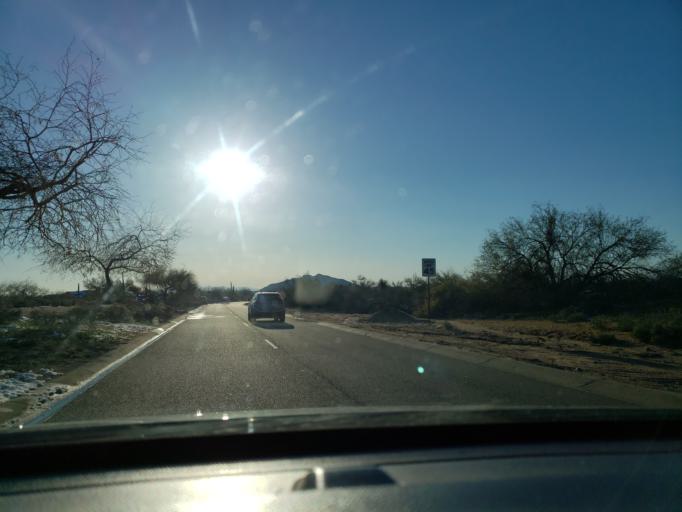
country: US
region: Arizona
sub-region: Maricopa County
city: Carefree
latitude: 33.8288
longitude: -111.8576
